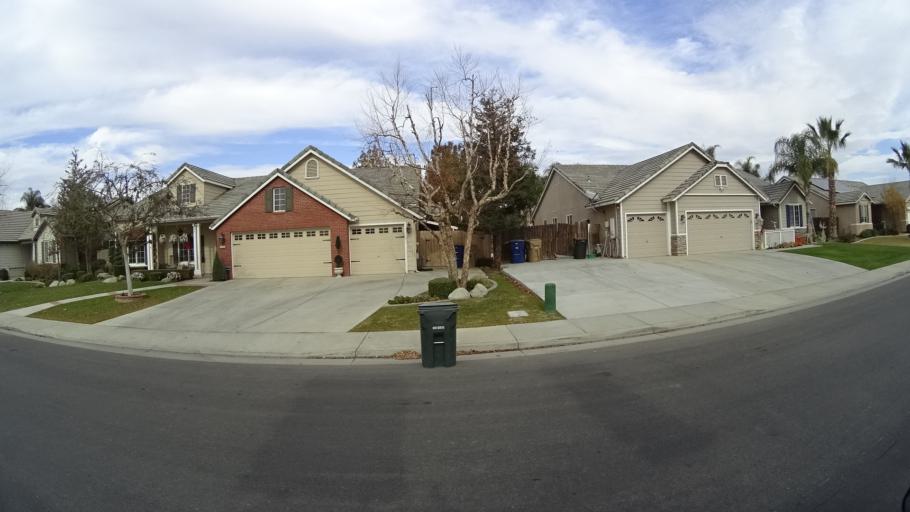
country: US
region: California
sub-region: Kern County
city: Rosedale
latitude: 35.4252
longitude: -119.1330
